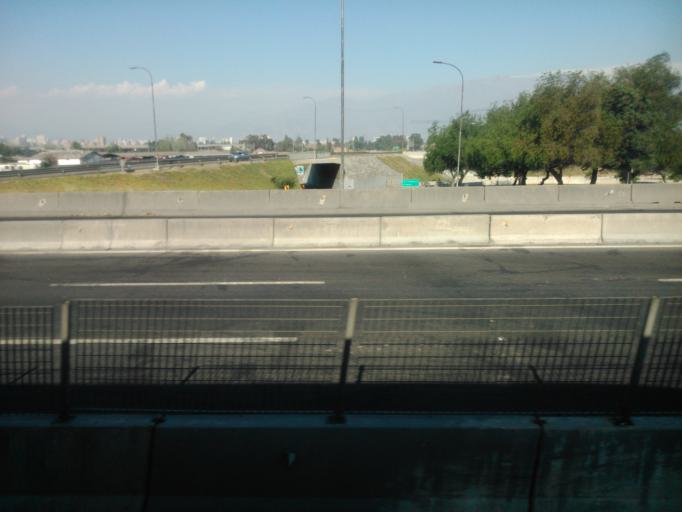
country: CL
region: Santiago Metropolitan
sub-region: Provincia de Santiago
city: Santiago
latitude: -33.4775
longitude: -70.6857
